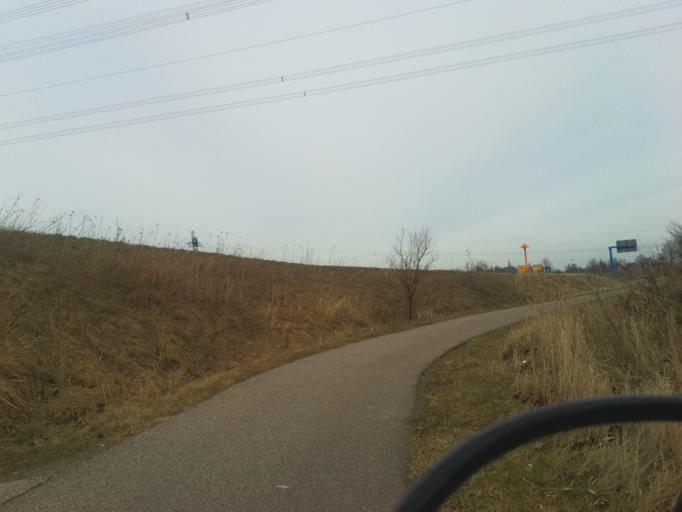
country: DE
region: Mecklenburg-Vorpommern
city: Bentwisch
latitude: 54.1084
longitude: 12.1907
